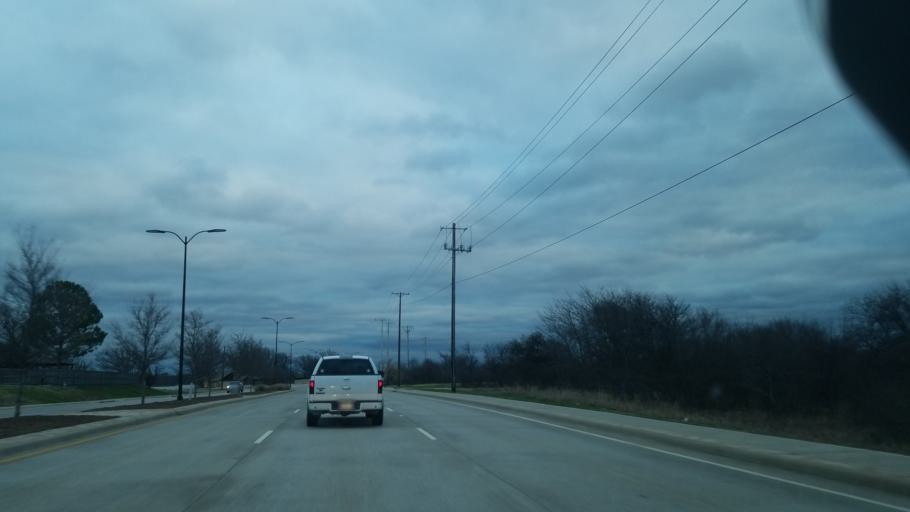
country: US
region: Texas
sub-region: Denton County
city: Little Elm
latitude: 33.1620
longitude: -96.9592
